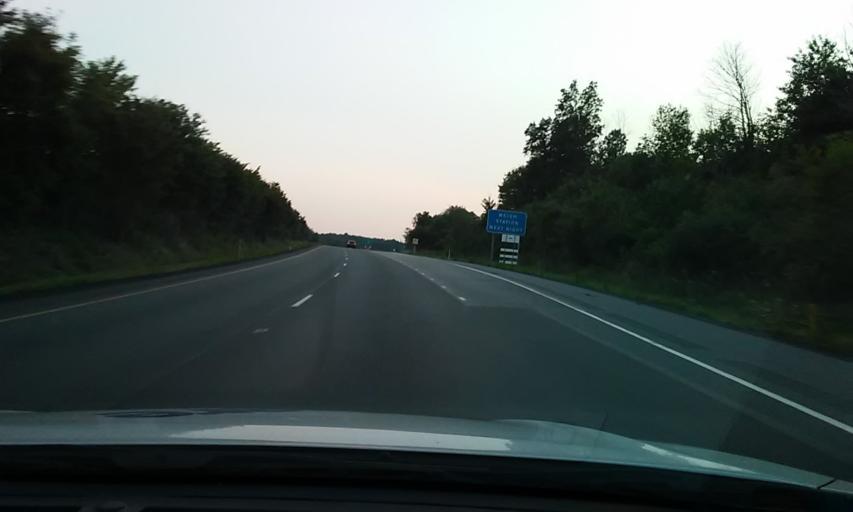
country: US
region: Pennsylvania
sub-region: Clarion County
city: Knox
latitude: 41.1994
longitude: -79.4957
